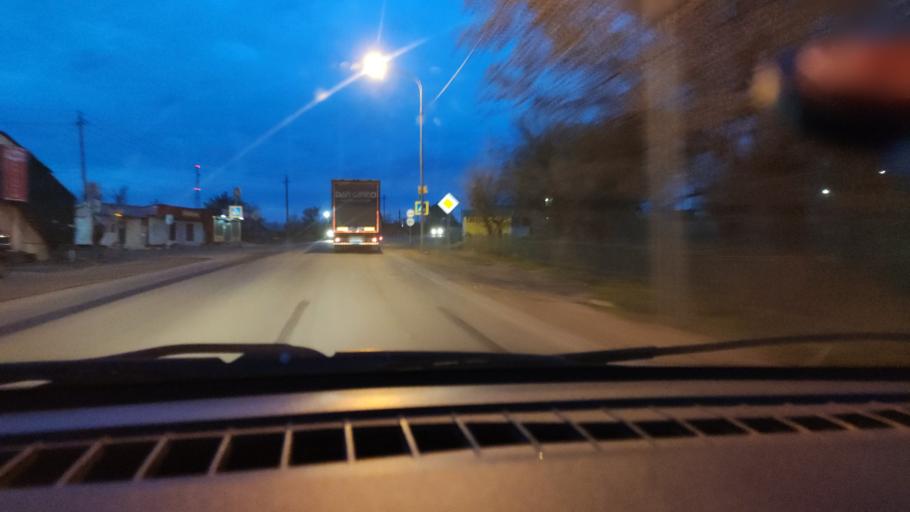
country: RU
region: Orenburg
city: Tatarskaya Kargala
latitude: 51.9473
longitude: 55.1758
